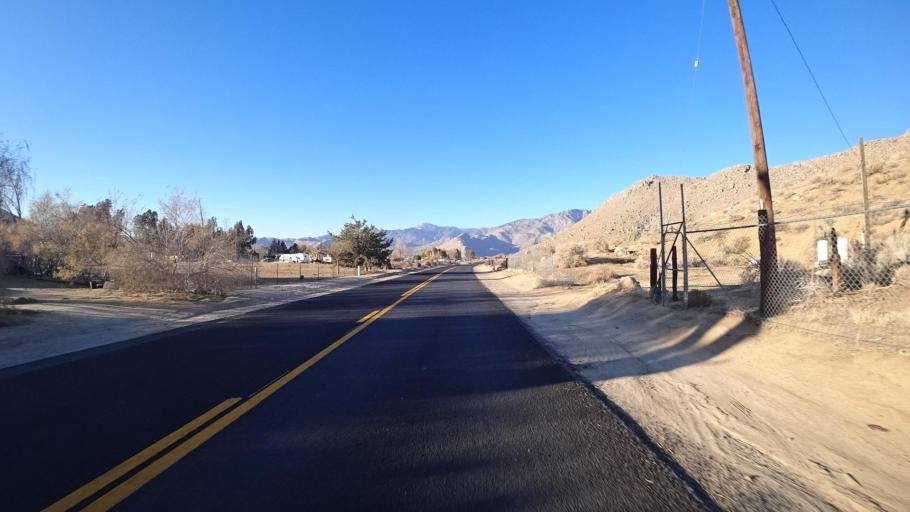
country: US
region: California
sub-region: Kern County
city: Weldon
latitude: 35.6405
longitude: -118.2486
